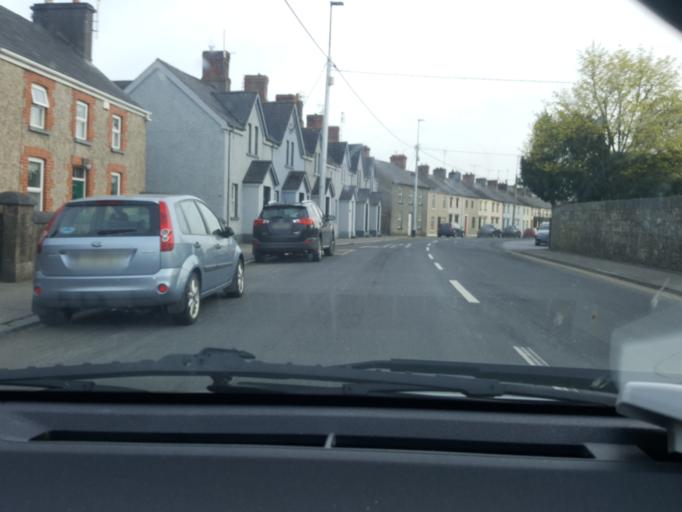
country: IE
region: Munster
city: Cahir
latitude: 52.3778
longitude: -7.9231
